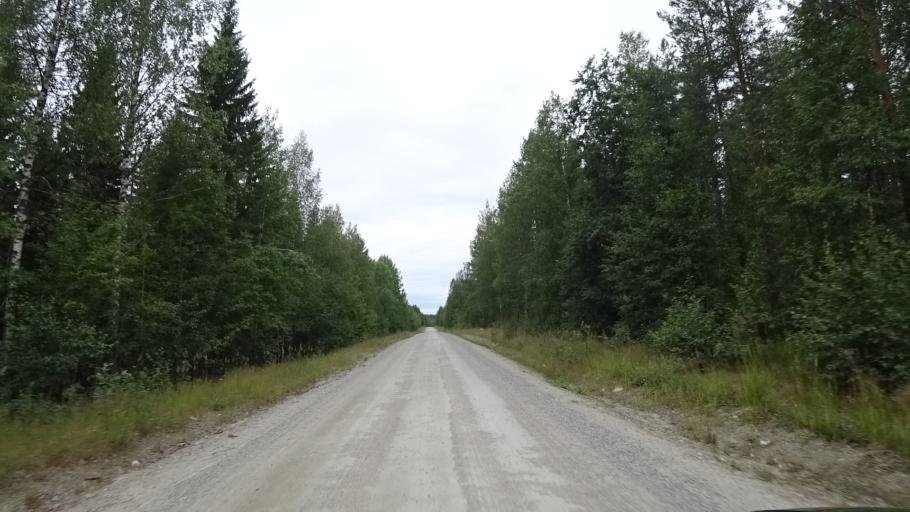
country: FI
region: North Karelia
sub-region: Joensuu
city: Eno
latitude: 63.1554
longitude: 30.6044
